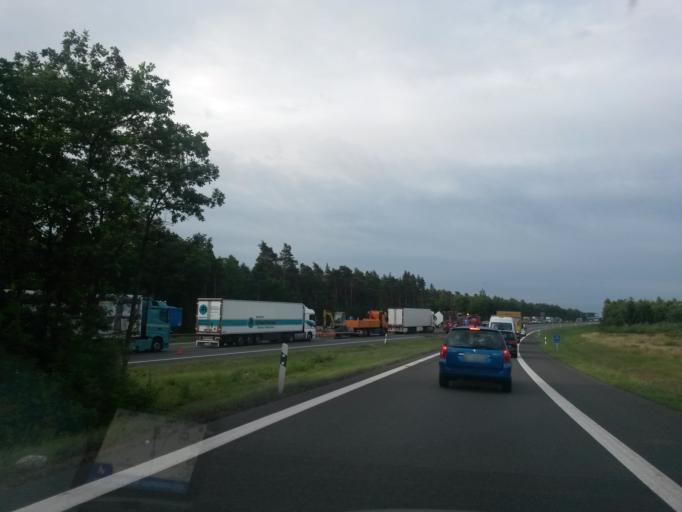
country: DE
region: Bavaria
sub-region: Regierungsbezirk Mittelfranken
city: Feucht
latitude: 49.3486
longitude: 11.2032
